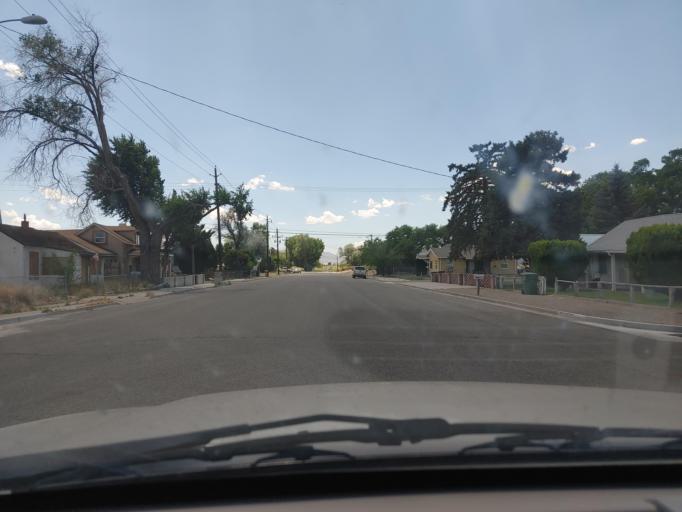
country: US
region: Nevada
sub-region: Humboldt County
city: Winnemucca
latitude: 40.9707
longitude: -117.7403
